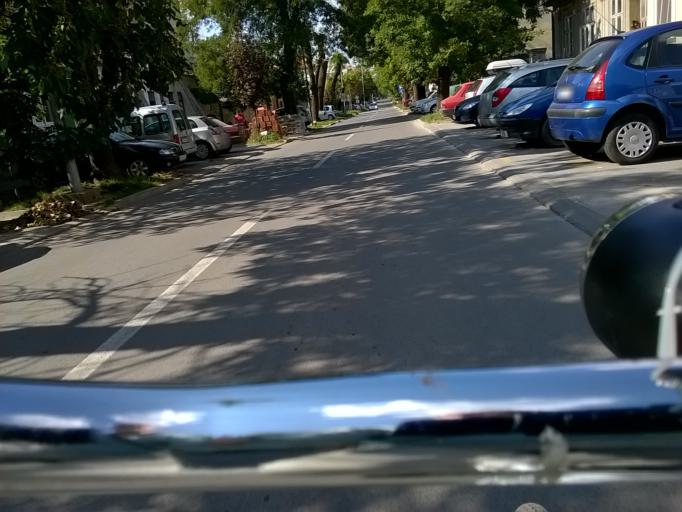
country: RS
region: Autonomna Pokrajina Vojvodina
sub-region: Juznobanatski Okrug
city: Pancevo
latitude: 44.8740
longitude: 20.6423
